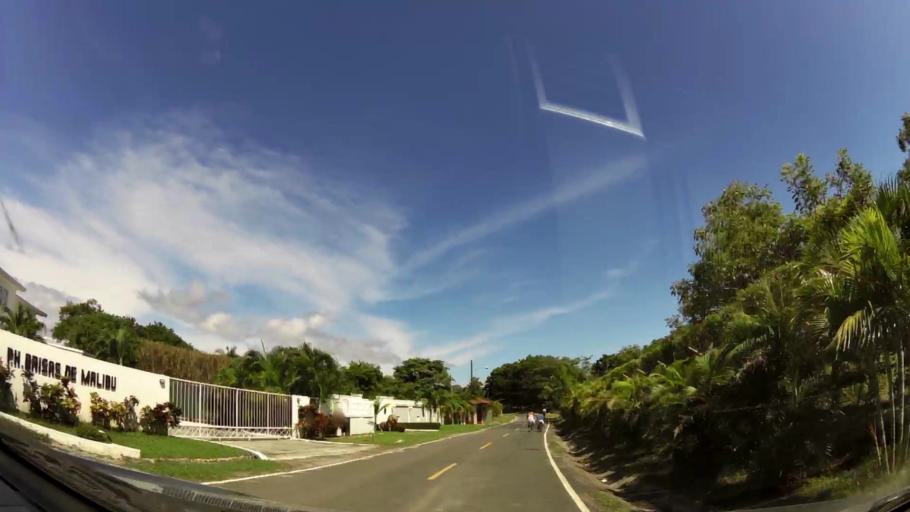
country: PA
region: Panama
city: Nueva Gorgona
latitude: 8.5588
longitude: -79.8689
